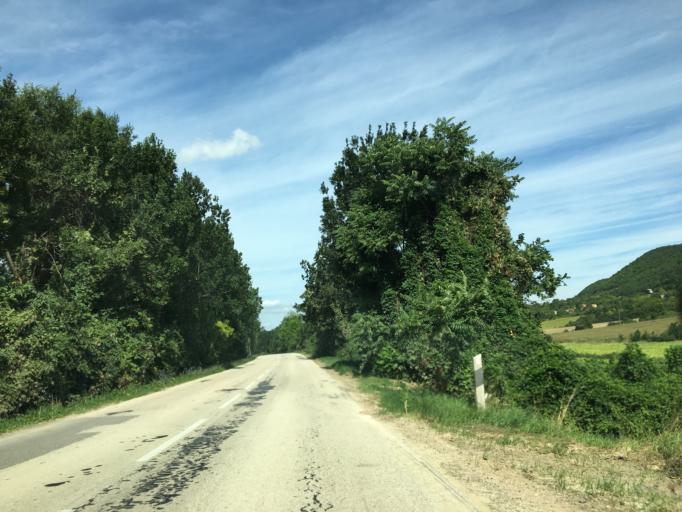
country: HU
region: Komarom-Esztergom
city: Bajna
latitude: 47.6268
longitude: 18.6250
